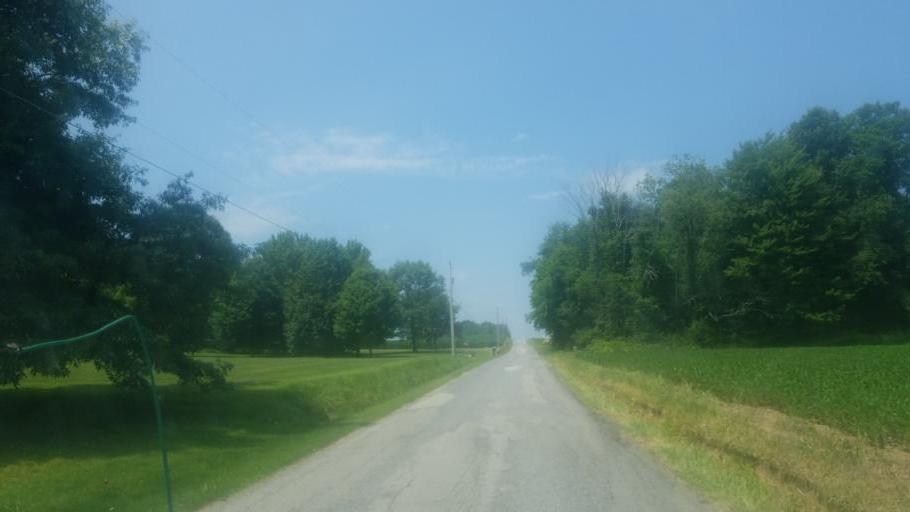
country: US
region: Ohio
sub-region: Columbiana County
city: Columbiana
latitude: 40.9225
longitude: -80.7081
